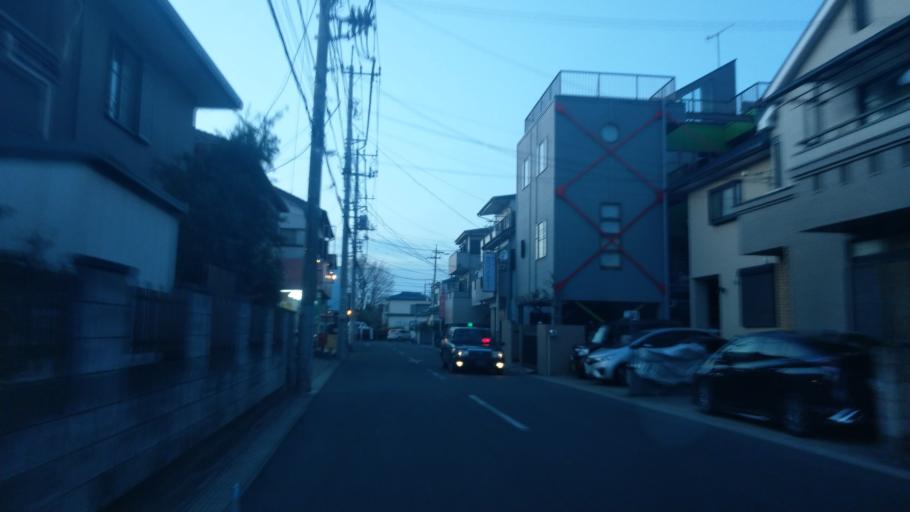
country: JP
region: Saitama
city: Yono
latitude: 35.8884
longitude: 139.6041
